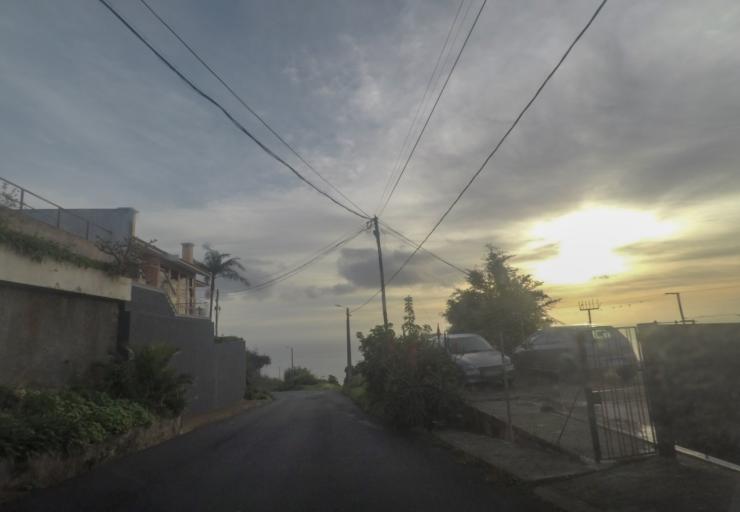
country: PT
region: Madeira
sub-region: Funchal
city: Nossa Senhora do Monte
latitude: 32.6561
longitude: -16.8768
